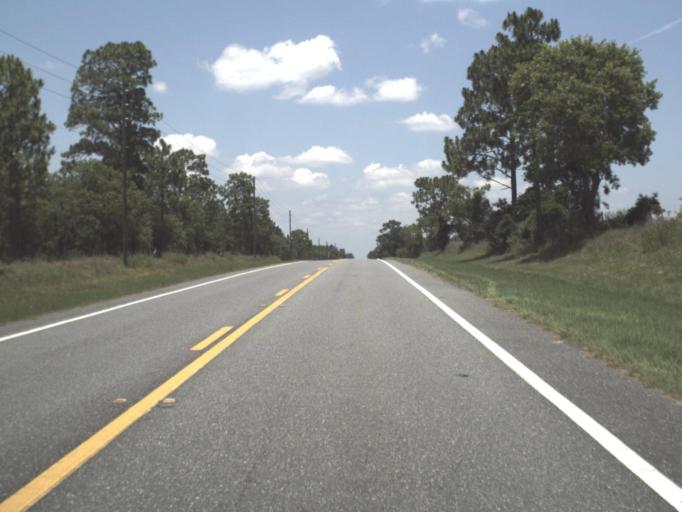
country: US
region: Florida
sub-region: Levy County
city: Williston Highlands
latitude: 29.2413
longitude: -82.5569
